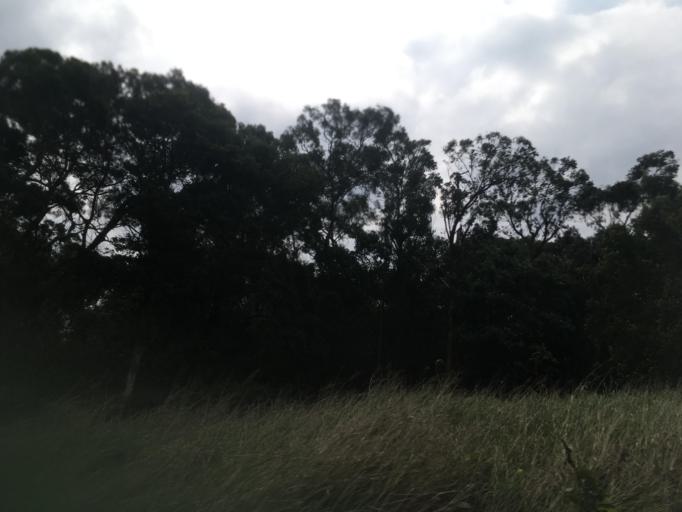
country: TW
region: Taiwan
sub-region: Miaoli
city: Miaoli
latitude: 24.4423
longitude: 120.7056
